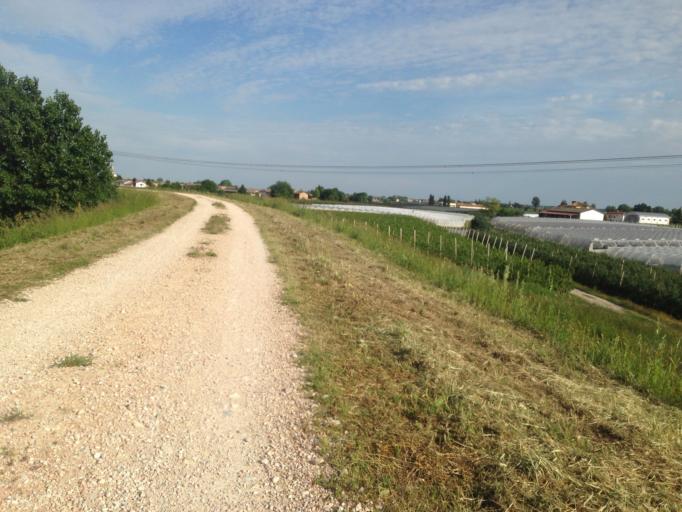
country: IT
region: Veneto
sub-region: Provincia di Verona
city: Belfiore
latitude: 45.3685
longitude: 11.1751
